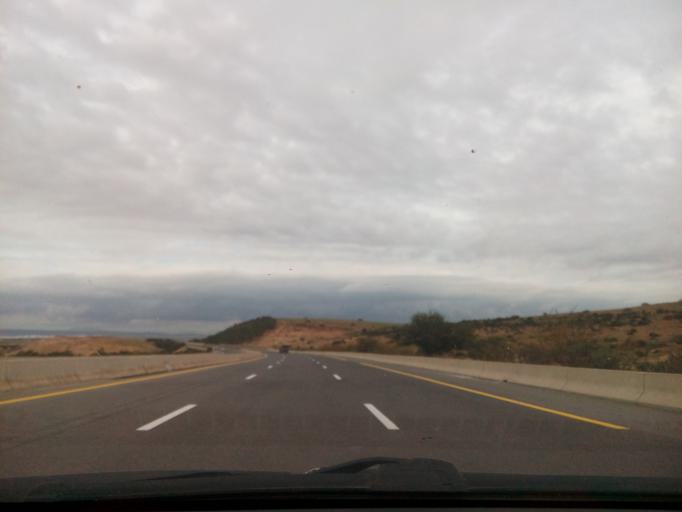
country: DZ
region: Sidi Bel Abbes
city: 'Ain el Berd
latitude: 35.4778
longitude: -0.3847
